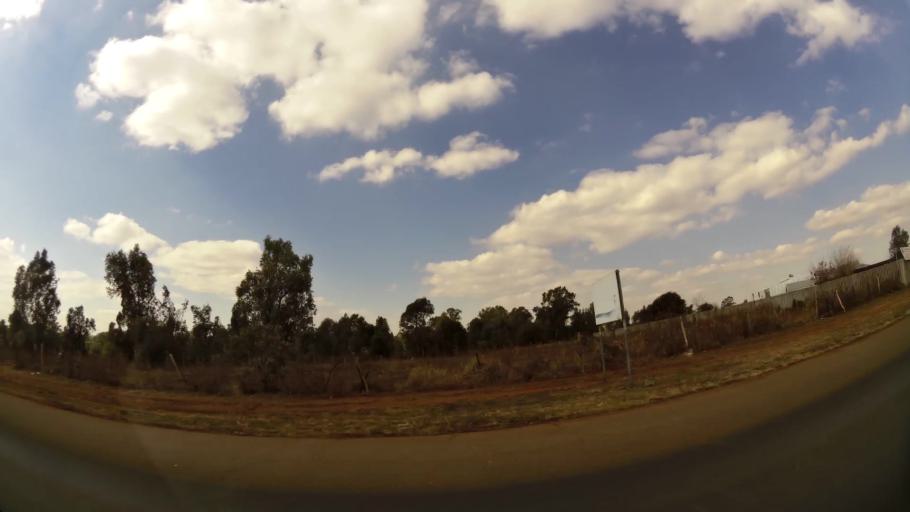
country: ZA
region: Gauteng
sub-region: Ekurhuleni Metropolitan Municipality
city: Tembisa
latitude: -25.9801
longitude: 28.2406
